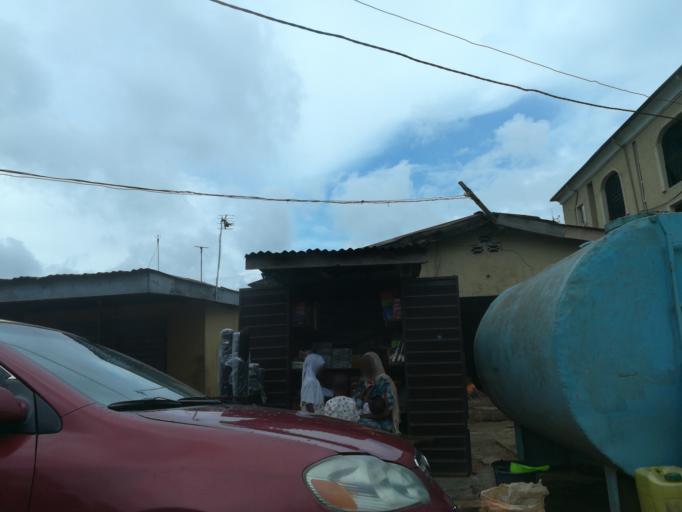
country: NG
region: Lagos
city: Agege
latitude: 6.6096
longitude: 3.3155
